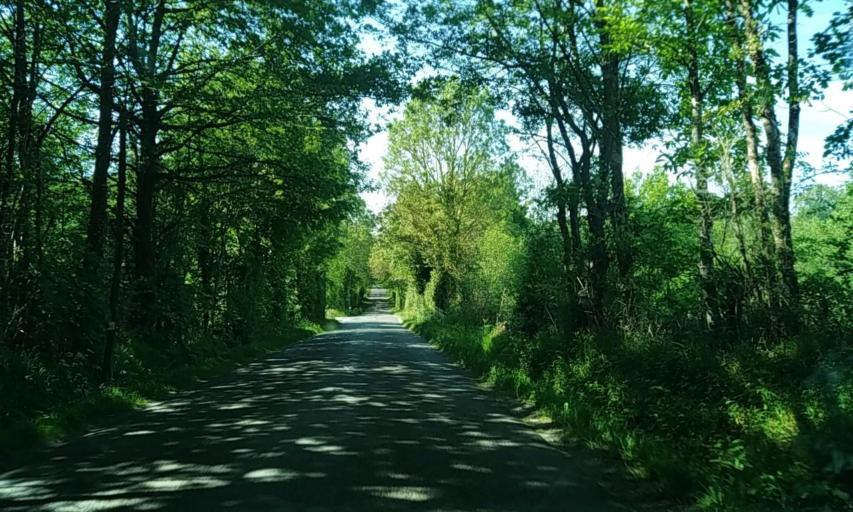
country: FR
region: Poitou-Charentes
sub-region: Departement des Deux-Sevres
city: Boisme
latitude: 46.7805
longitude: -0.4459
